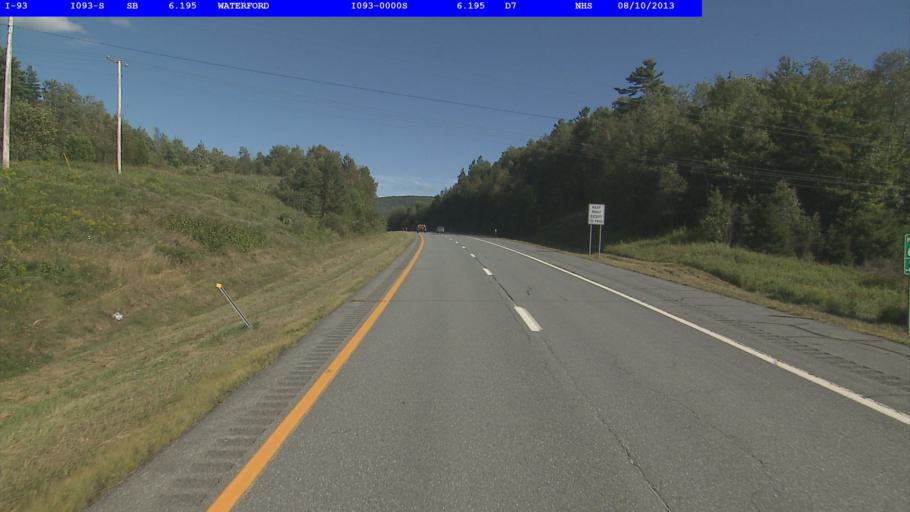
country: US
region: Vermont
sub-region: Caledonia County
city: Saint Johnsbury
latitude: 44.4204
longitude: -71.9345
